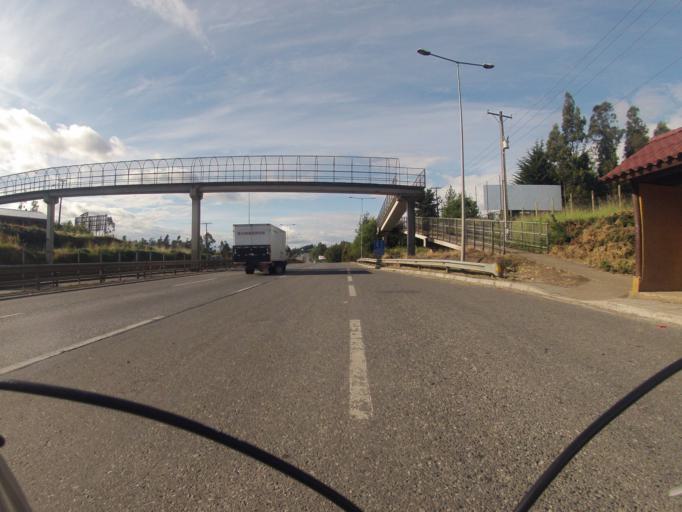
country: CL
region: Araucania
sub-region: Provincia de Cautin
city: Temuco
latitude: -38.8197
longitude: -72.6233
